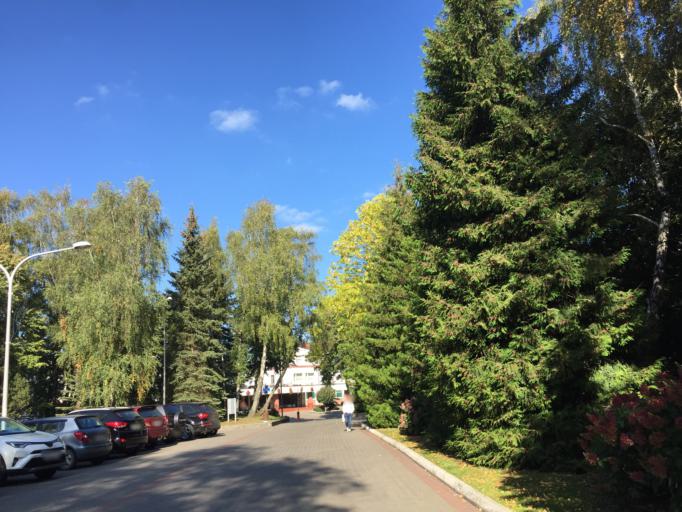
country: RU
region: Kaliningrad
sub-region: Gorod Svetlogorsk
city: Svetlogorsk
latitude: 54.9423
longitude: 20.1350
